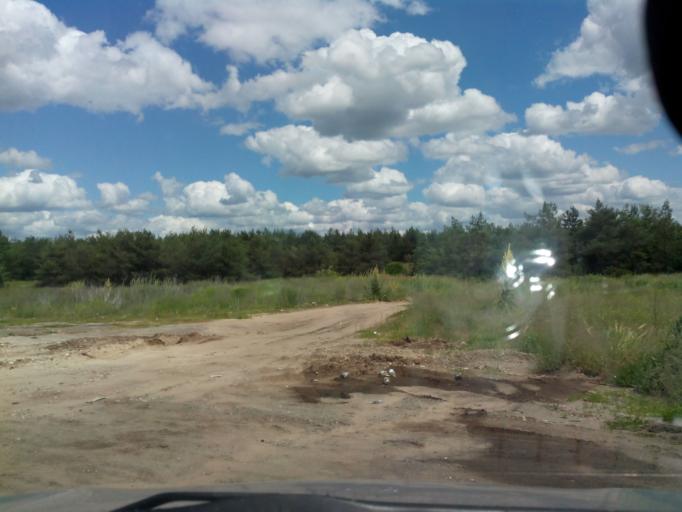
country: RU
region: Volgograd
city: Ilovlya
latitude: 49.2283
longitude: 44.0757
